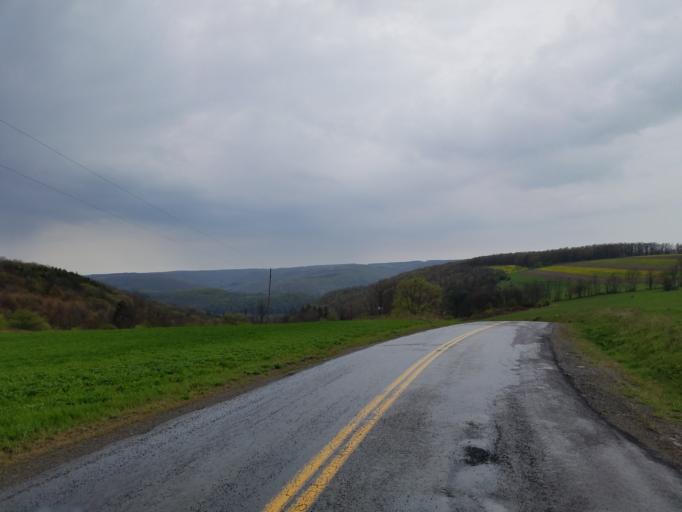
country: US
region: New York
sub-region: Steuben County
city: Canisteo
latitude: 42.1417
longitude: -77.6102
